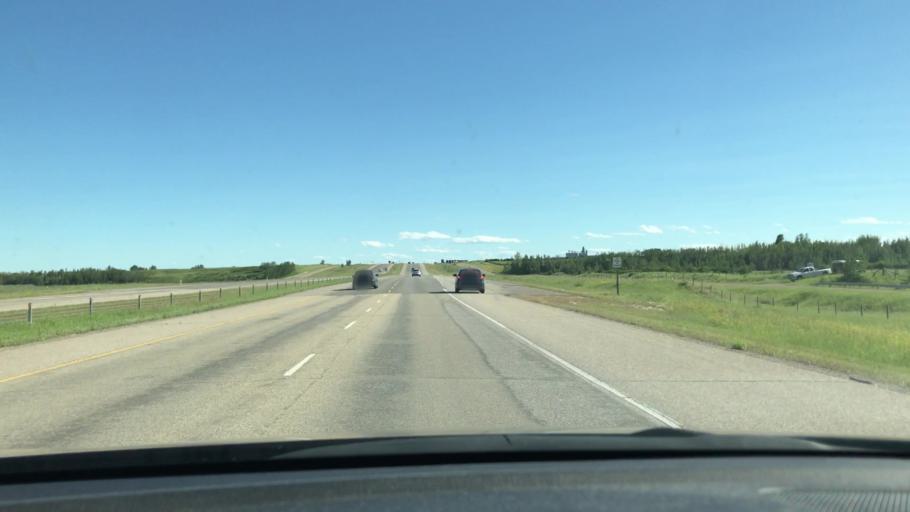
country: CA
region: Alberta
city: Crossfield
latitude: 51.5193
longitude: -114.0253
